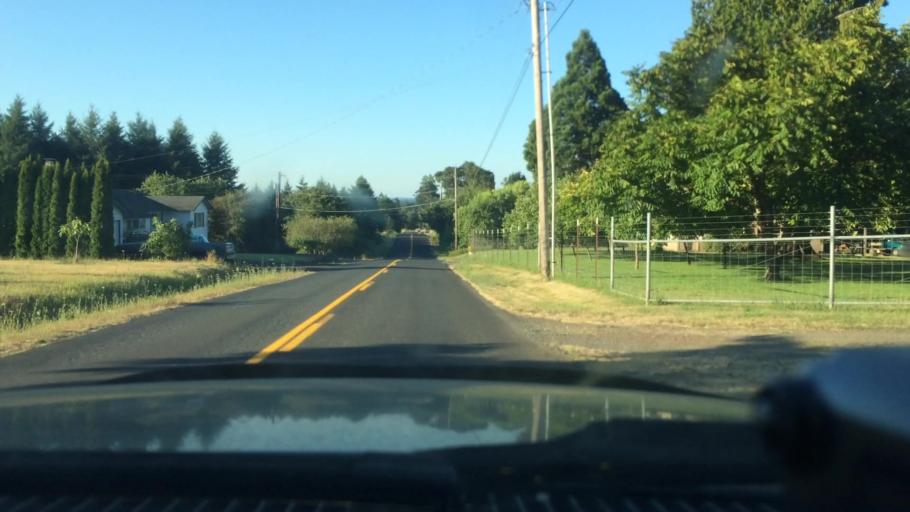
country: US
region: Oregon
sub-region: Yamhill County
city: Newberg
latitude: 45.3261
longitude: -122.9404
